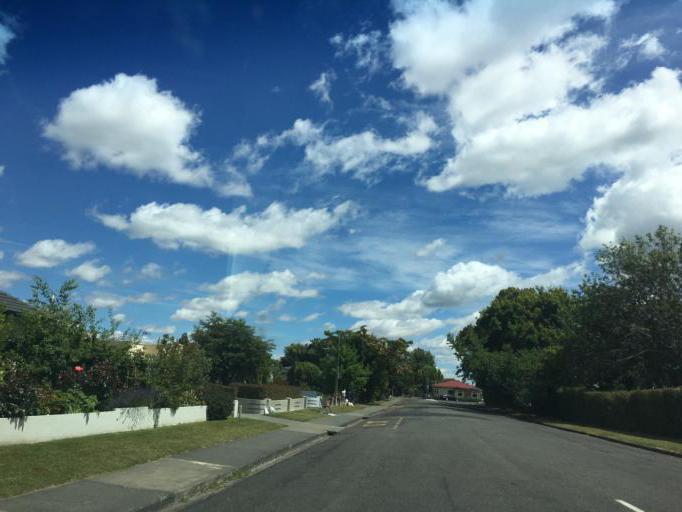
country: NZ
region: Hawke's Bay
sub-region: Hastings District
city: Hastings
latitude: -39.6494
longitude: 176.8605
